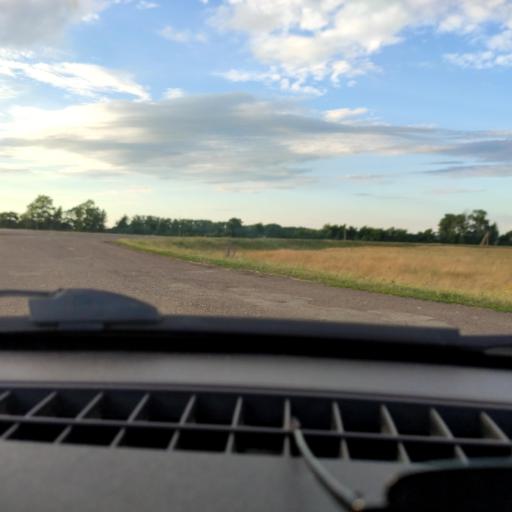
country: RU
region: Bashkortostan
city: Chishmy
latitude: 54.3773
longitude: 55.4245
